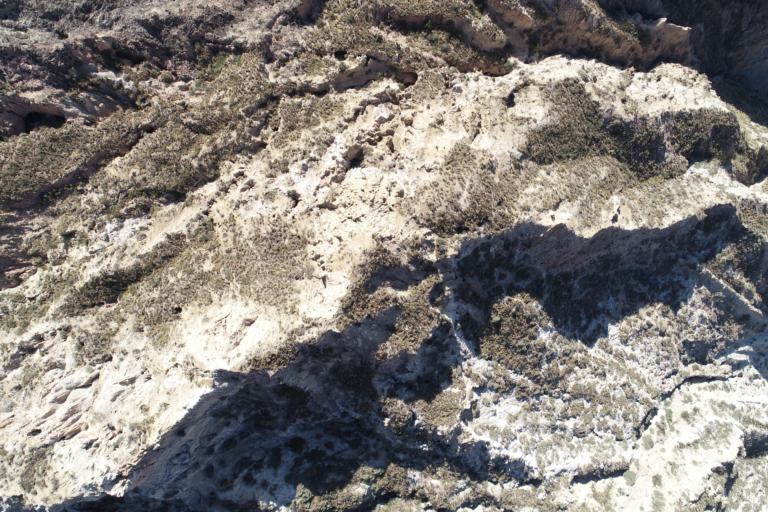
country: BO
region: La Paz
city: La Paz
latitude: -16.5515
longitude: -68.1070
